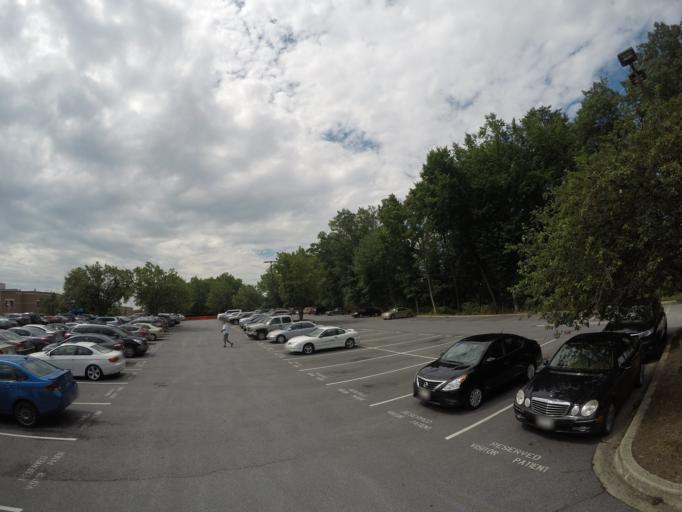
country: US
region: Maryland
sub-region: Prince George's County
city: Goddard
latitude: 38.9831
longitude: -76.8661
